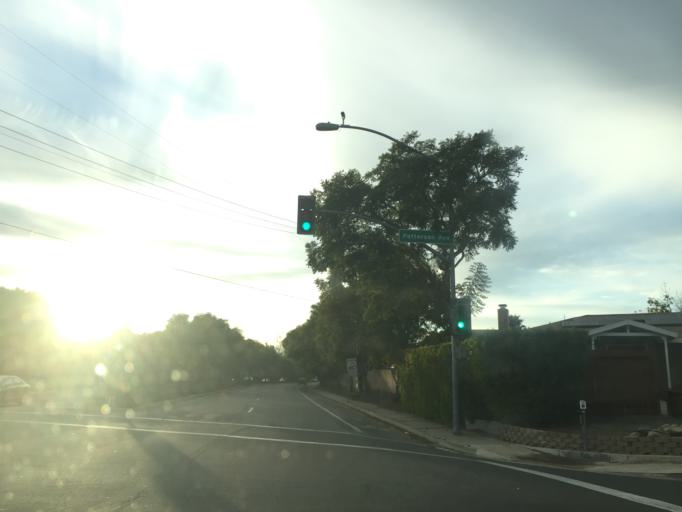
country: US
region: California
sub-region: Santa Barbara County
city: Goleta
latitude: 34.4532
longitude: -119.8080
